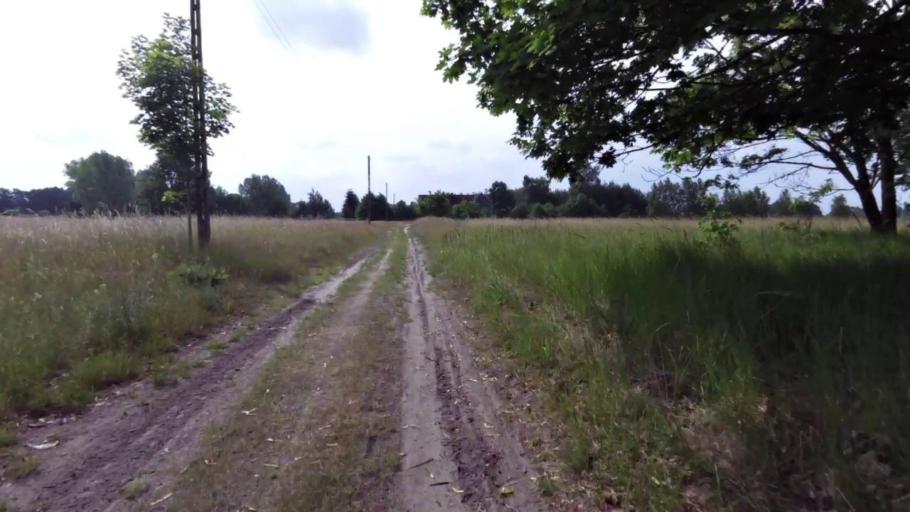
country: PL
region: West Pomeranian Voivodeship
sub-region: Powiat kamienski
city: Wolin
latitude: 53.7591
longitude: 14.6500
